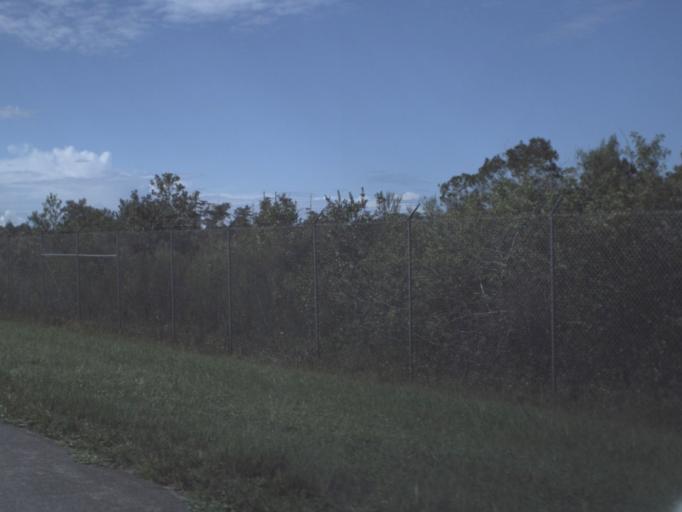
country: US
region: Florida
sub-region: Collier County
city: Lely Resort
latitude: 25.9884
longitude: -81.3476
